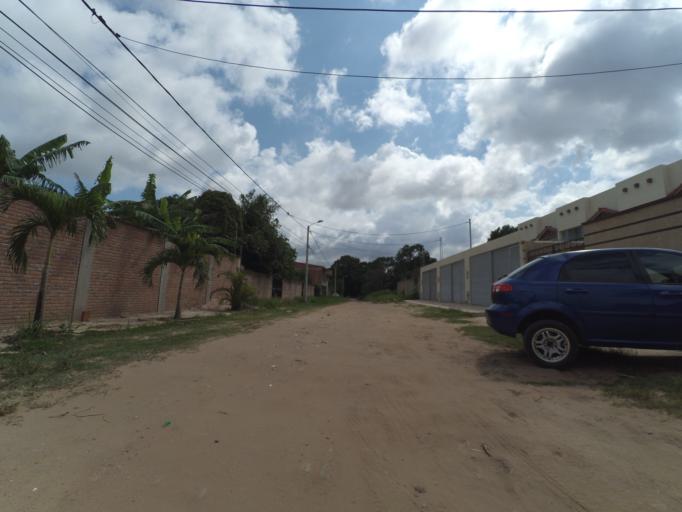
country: BO
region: Santa Cruz
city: Santa Cruz de la Sierra
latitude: -17.8075
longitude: -63.2261
